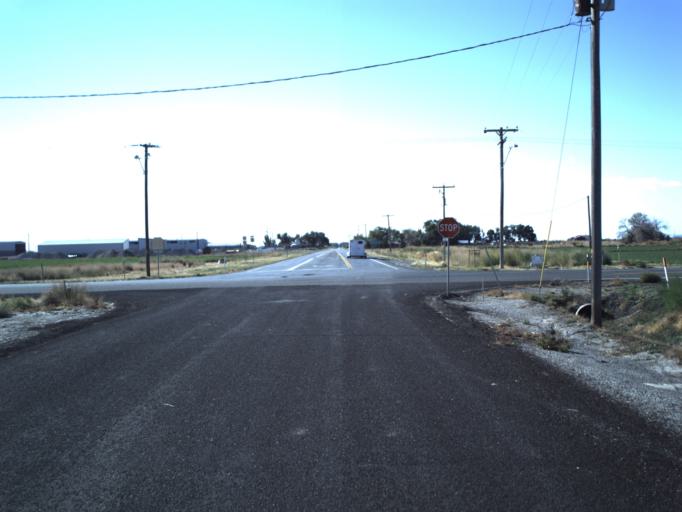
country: US
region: Utah
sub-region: Millard County
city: Delta
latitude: 39.3312
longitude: -112.6523
